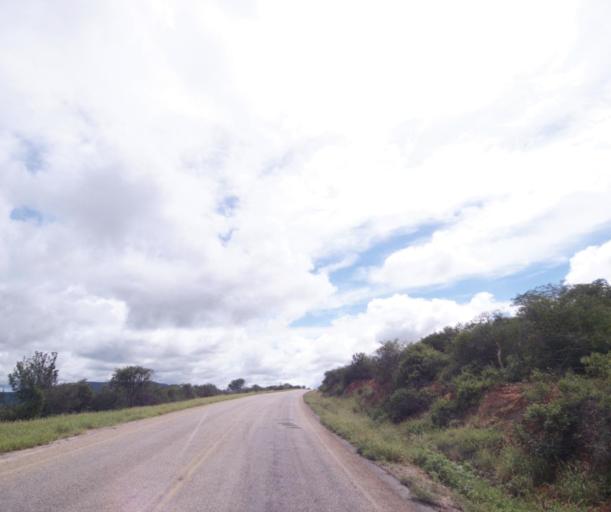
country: BR
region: Bahia
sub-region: Brumado
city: Brumado
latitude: -14.2003
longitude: -41.6166
